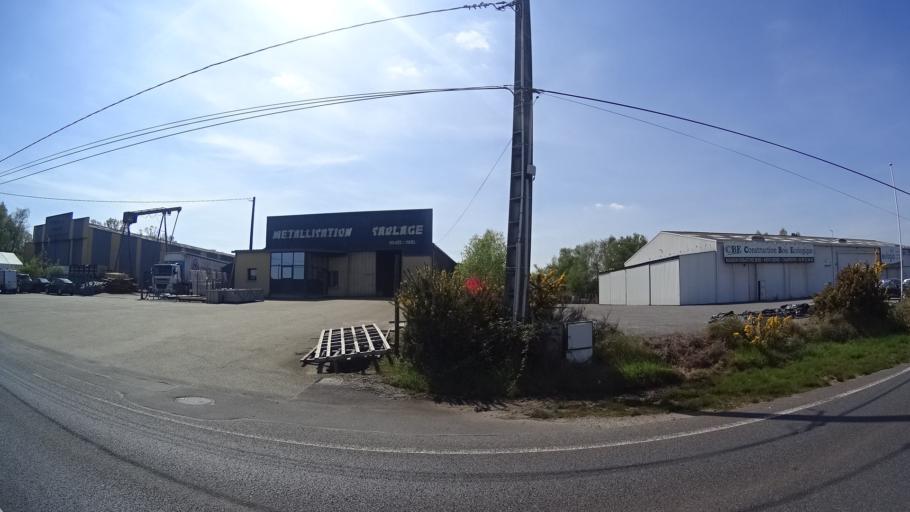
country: FR
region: Pays de la Loire
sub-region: Departement de la Loire-Atlantique
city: Saint-Nicolas-de-Redon
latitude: 47.6292
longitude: -2.0495
